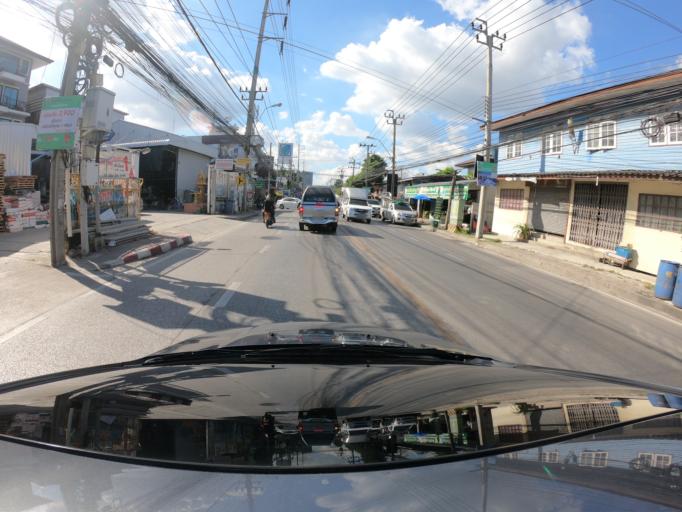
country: TH
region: Bangkok
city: Bang Na
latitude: 13.6542
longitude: 100.6123
